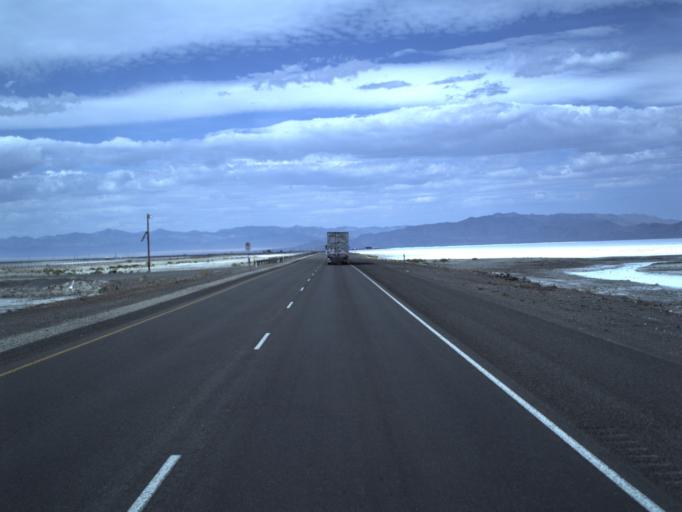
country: US
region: Utah
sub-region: Tooele County
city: Wendover
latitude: 40.7388
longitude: -113.8201
